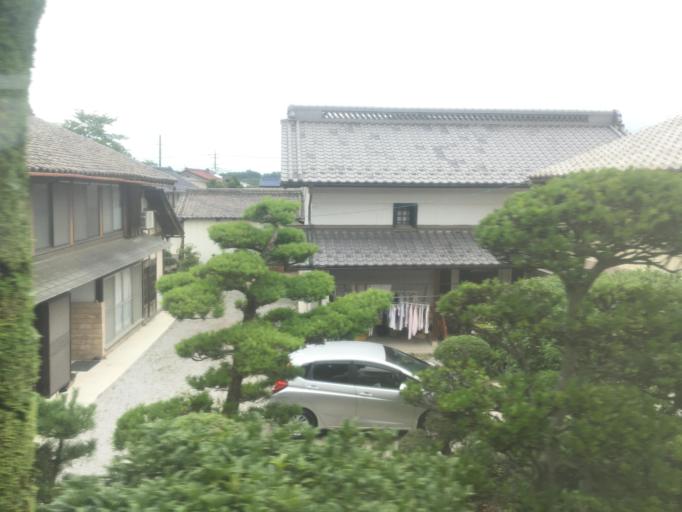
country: JP
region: Gunma
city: Takasaki
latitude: 36.2898
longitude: 139.0204
